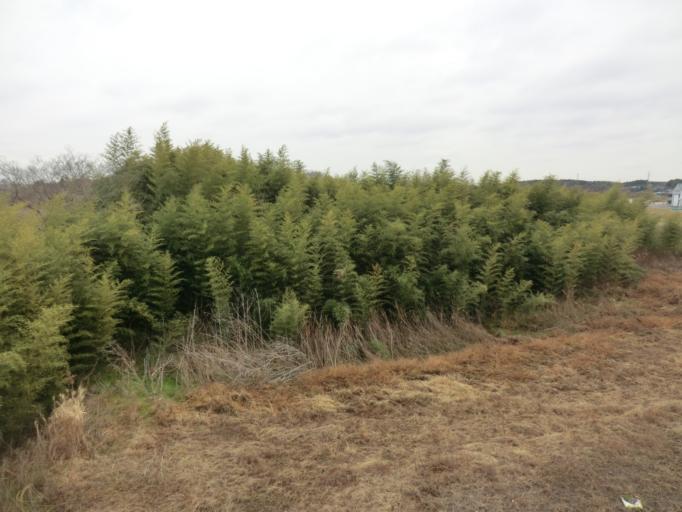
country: JP
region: Ibaraki
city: Naka
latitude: 36.1200
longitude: 140.1311
